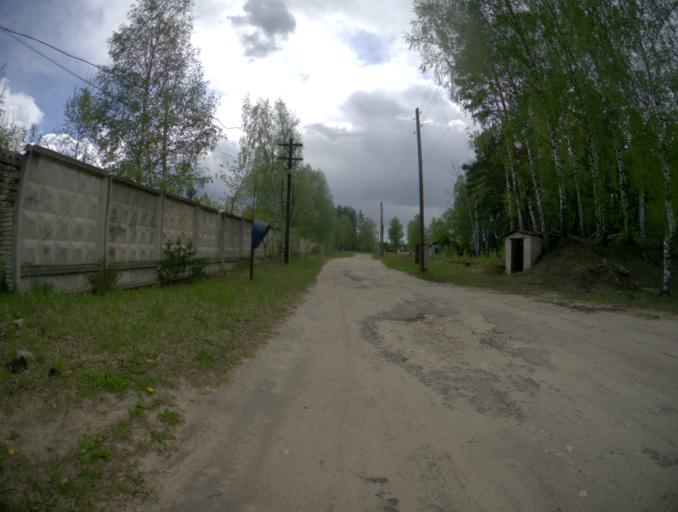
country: RU
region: Vladimir
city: Velikodvorskiy
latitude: 55.2383
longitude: 40.6518
